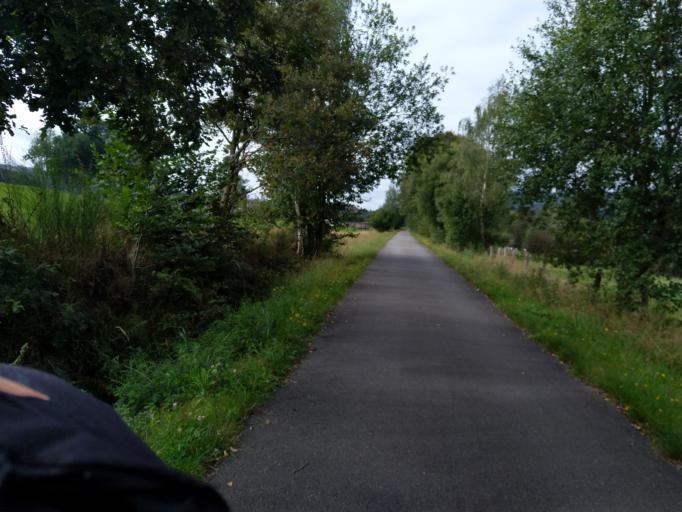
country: BE
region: Wallonia
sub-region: Province de Liege
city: Stavelot
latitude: 50.4057
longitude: 5.9613
